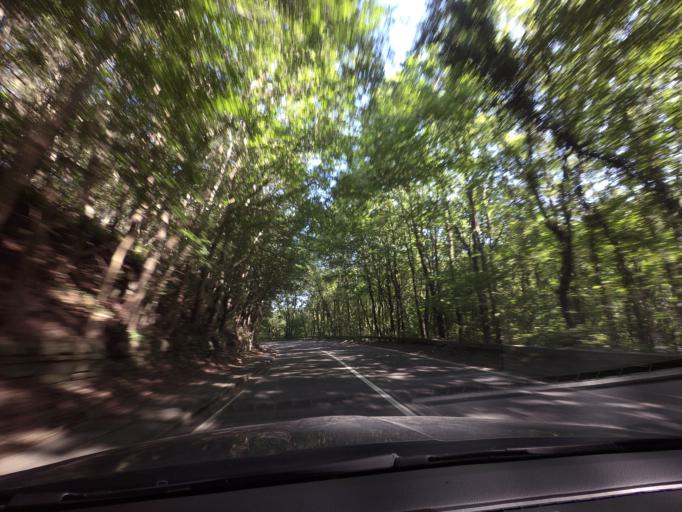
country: GB
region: England
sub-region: Derbyshire
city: Bakewell
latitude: 53.2459
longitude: -1.5893
